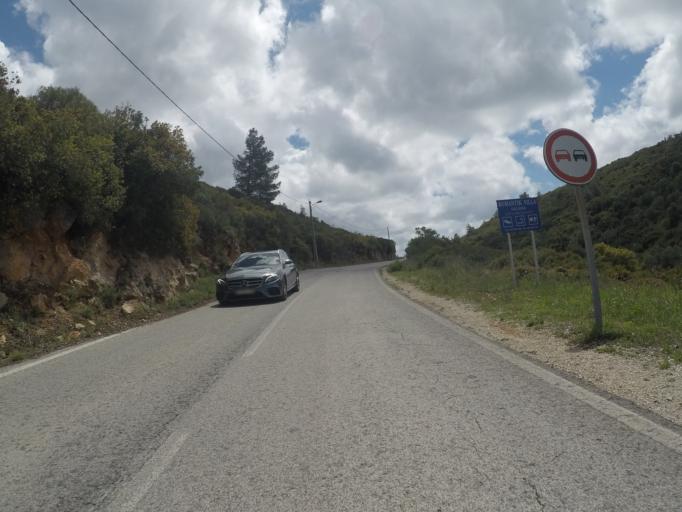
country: PT
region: Faro
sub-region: Vila do Bispo
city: Vila do Bispo
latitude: 37.0707
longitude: -8.8266
